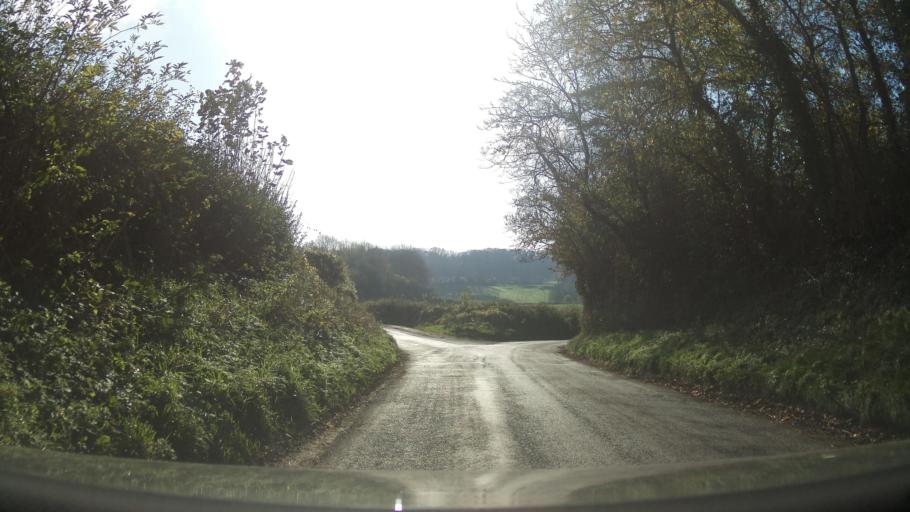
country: GB
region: England
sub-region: Somerset
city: Castle Cary
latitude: 51.0666
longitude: -2.4759
